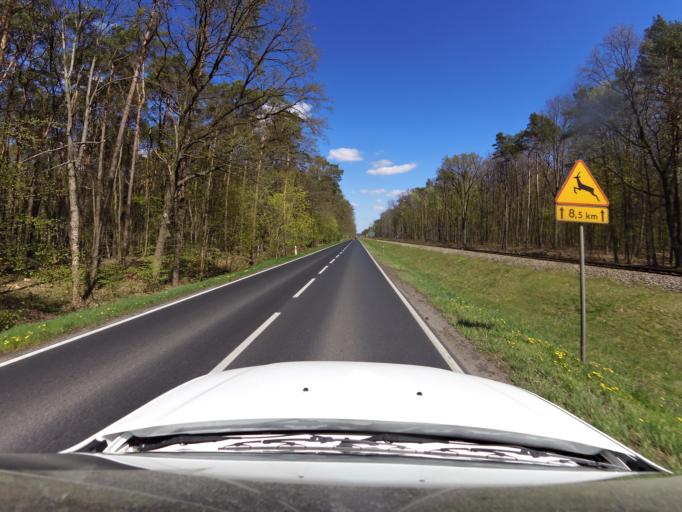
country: PL
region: West Pomeranian Voivodeship
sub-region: Powiat mysliborski
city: Debno
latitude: 52.7447
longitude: 14.7167
